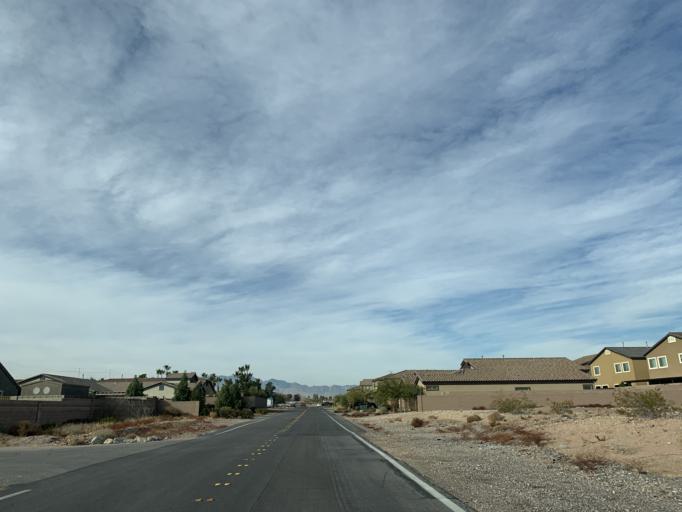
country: US
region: Nevada
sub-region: Clark County
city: Enterprise
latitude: 36.0045
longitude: -115.1838
